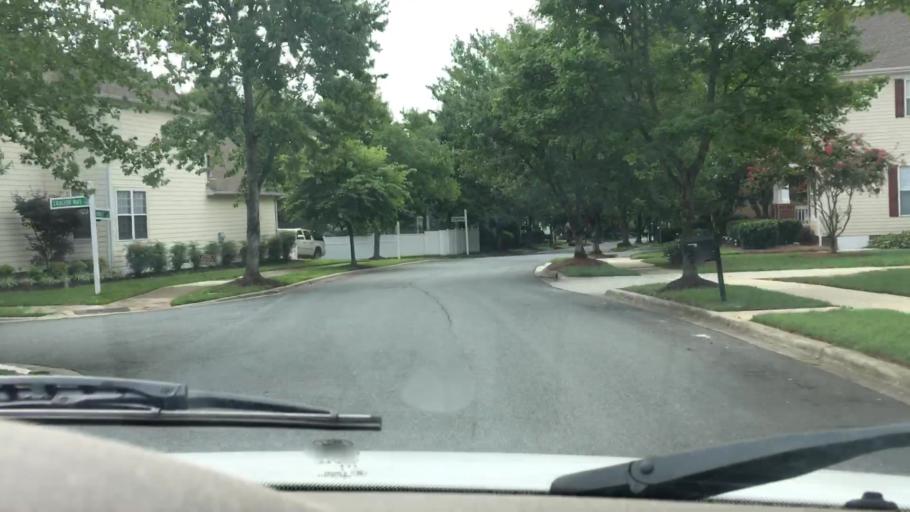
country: US
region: North Carolina
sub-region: Mecklenburg County
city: Cornelius
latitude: 35.4486
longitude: -80.8845
